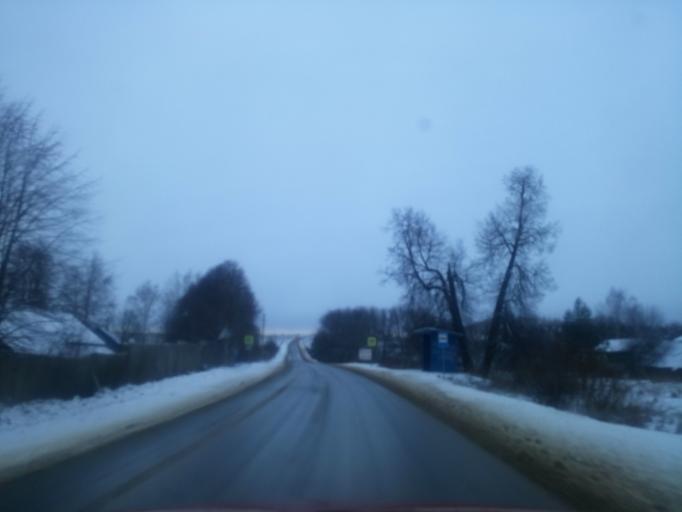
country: RU
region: Tverskaya
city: Likhoslavl'
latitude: 56.9704
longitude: 35.4329
